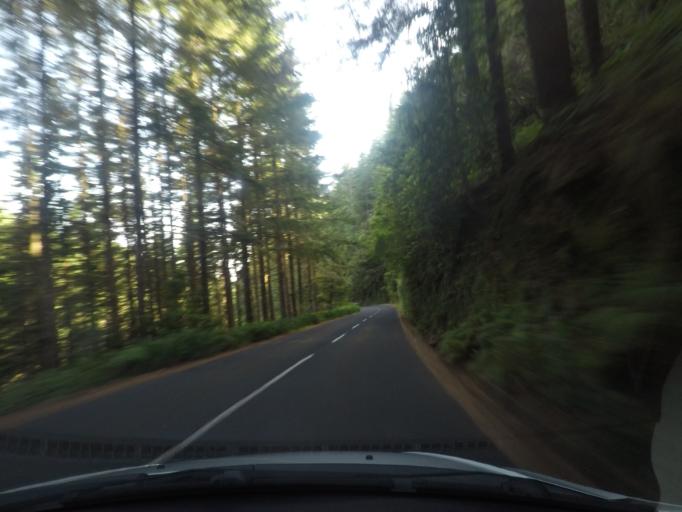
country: PT
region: Madeira
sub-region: Funchal
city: Nossa Senhora do Monte
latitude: 32.7213
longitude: -16.8893
